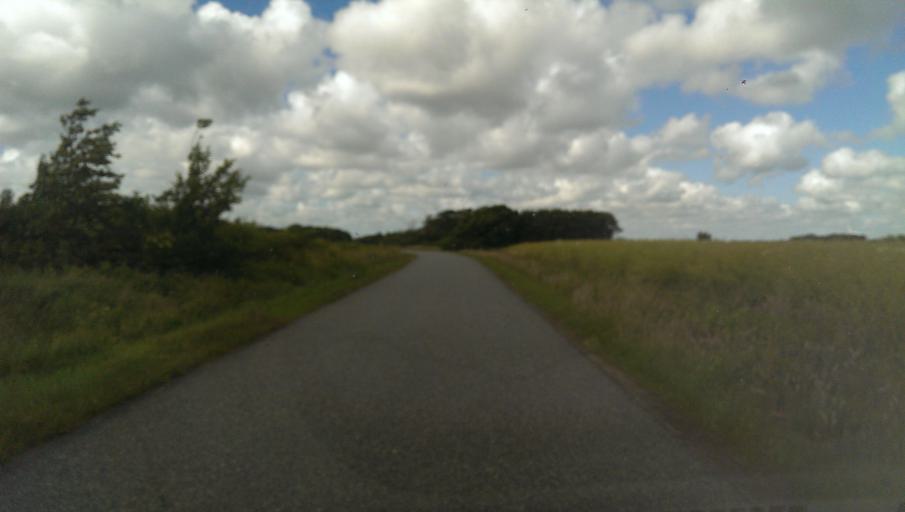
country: DK
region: Central Jutland
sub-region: Holstebro Kommune
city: Ulfborg
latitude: 56.2696
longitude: 8.2468
